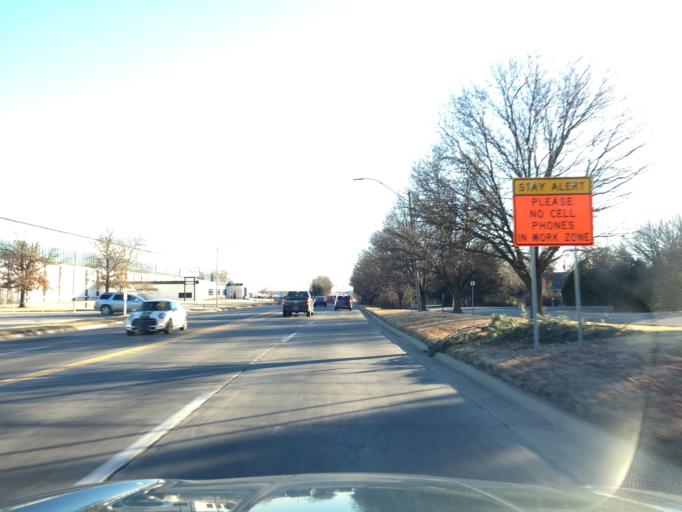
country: US
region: Kansas
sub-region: Sedgwick County
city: Bellaire
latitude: 37.6890
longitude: -97.2262
